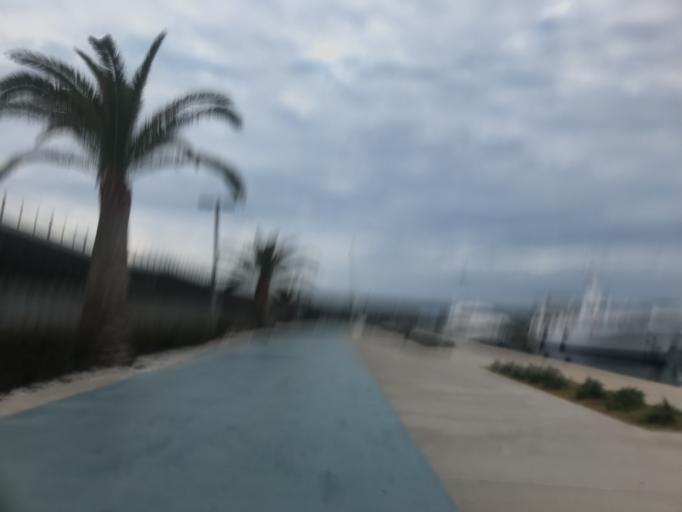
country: ES
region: Valencia
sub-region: Provincia de Valencia
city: Alboraya
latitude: 39.4624
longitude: -0.3134
